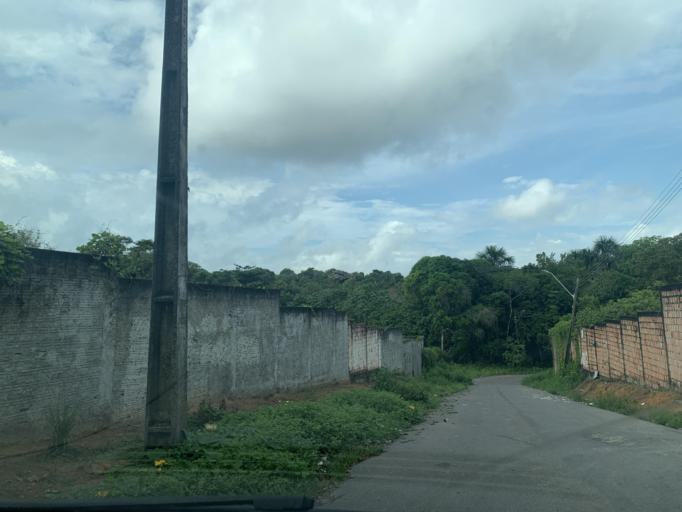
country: BR
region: Amazonas
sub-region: Manaus
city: Manaus
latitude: -3.0813
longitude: -59.9632
